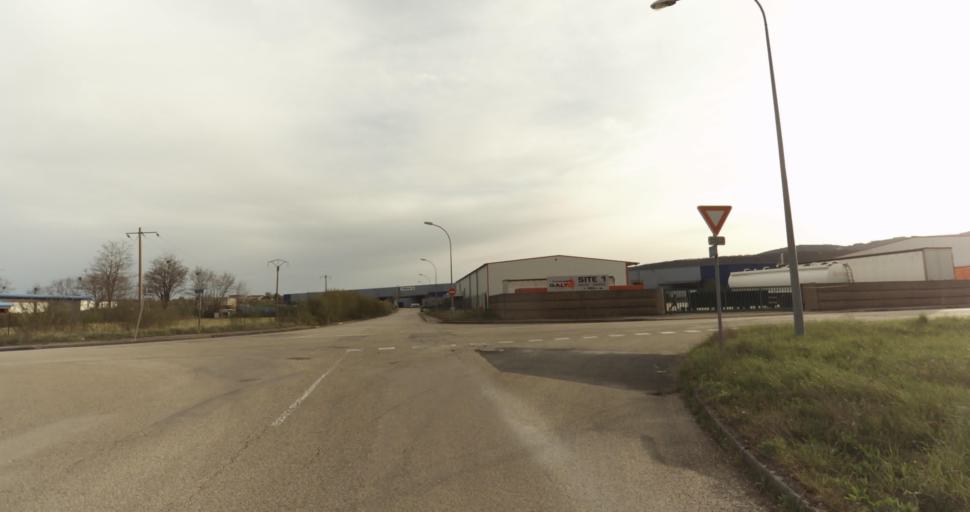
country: FR
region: Rhone-Alpes
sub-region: Departement de l'Ain
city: Amberieu-en-Bugey
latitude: 45.9655
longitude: 5.3436
